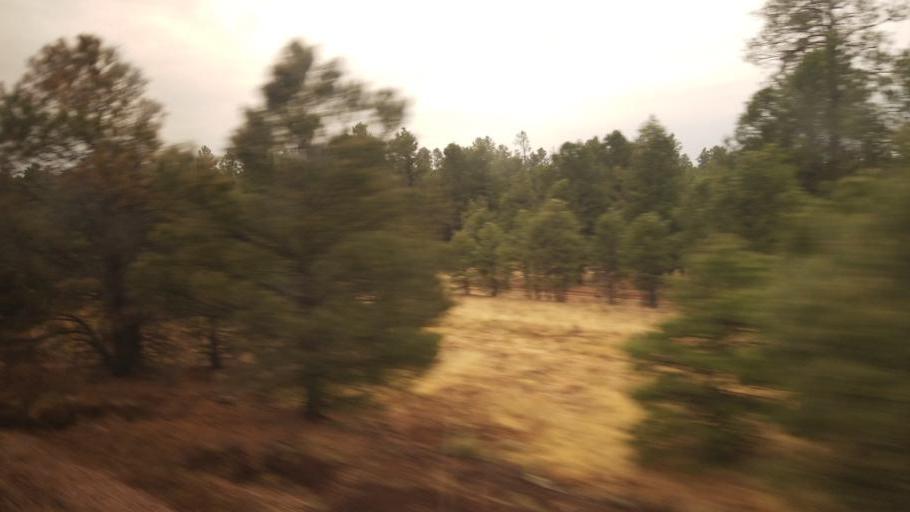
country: US
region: Arizona
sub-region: Coconino County
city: Parks
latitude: 35.2432
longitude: -111.8718
